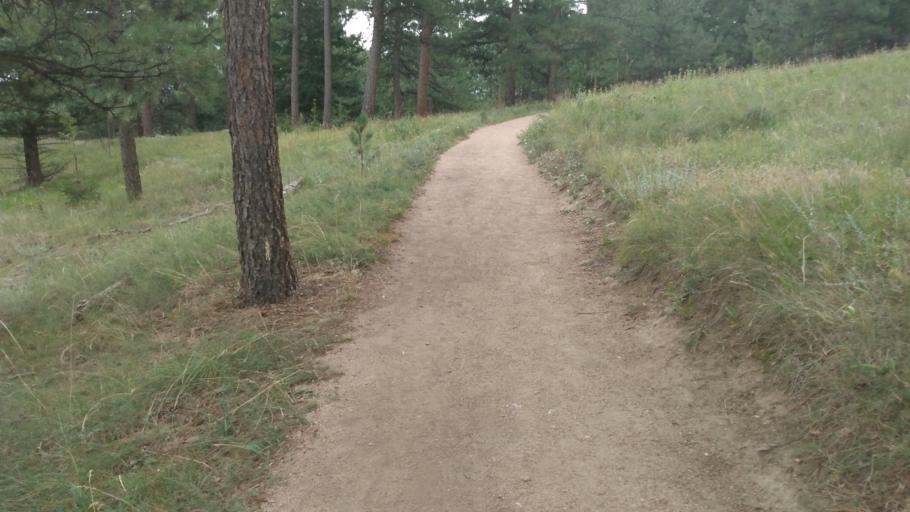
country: US
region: Colorado
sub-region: Boulder County
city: Boulder
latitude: 40.0027
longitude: -105.3059
